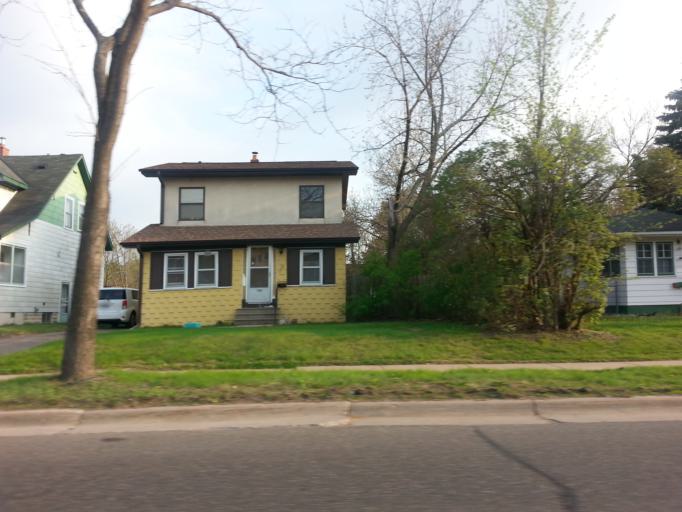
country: US
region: Minnesota
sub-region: Ramsey County
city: Maplewood
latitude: 44.9631
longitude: -93.0199
